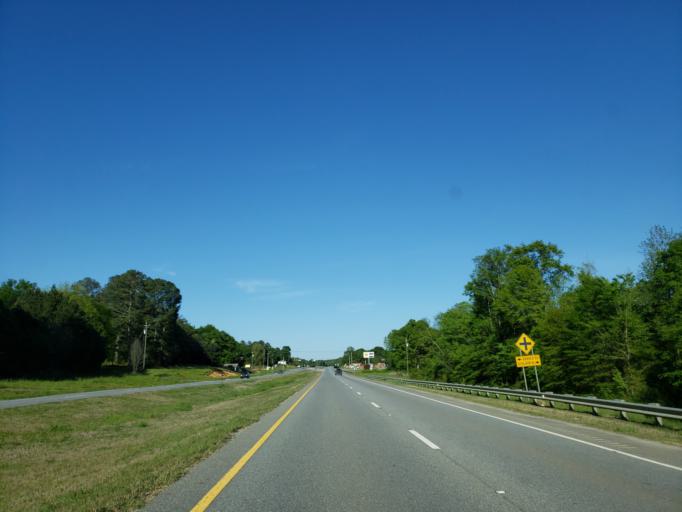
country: US
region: Georgia
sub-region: Polk County
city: Aragon
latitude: 34.0059
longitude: -85.1449
